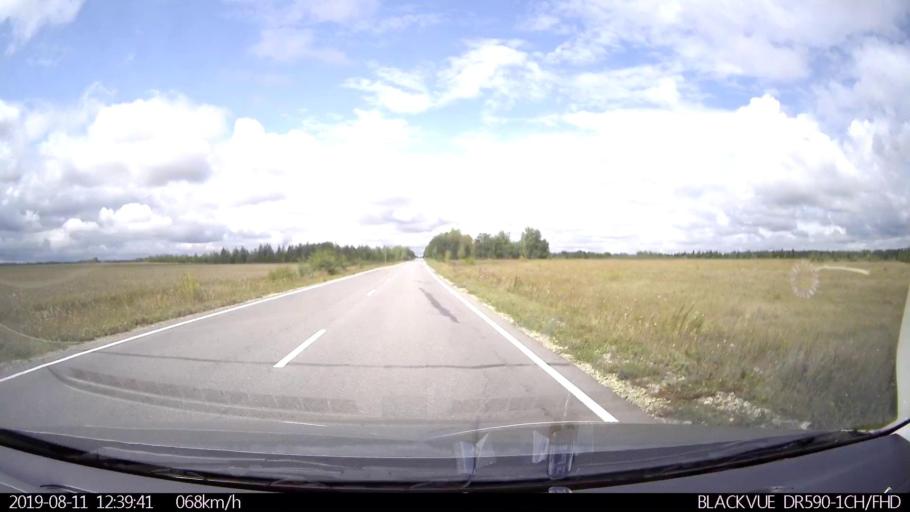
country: RU
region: Ulyanovsk
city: Ignatovka
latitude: 53.8345
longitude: 47.7920
